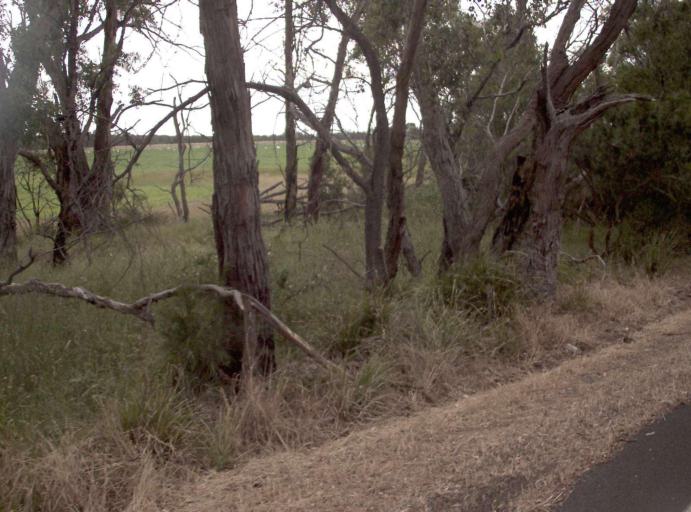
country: AU
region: Victoria
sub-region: Wellington
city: Sale
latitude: -38.3816
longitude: 146.9803
